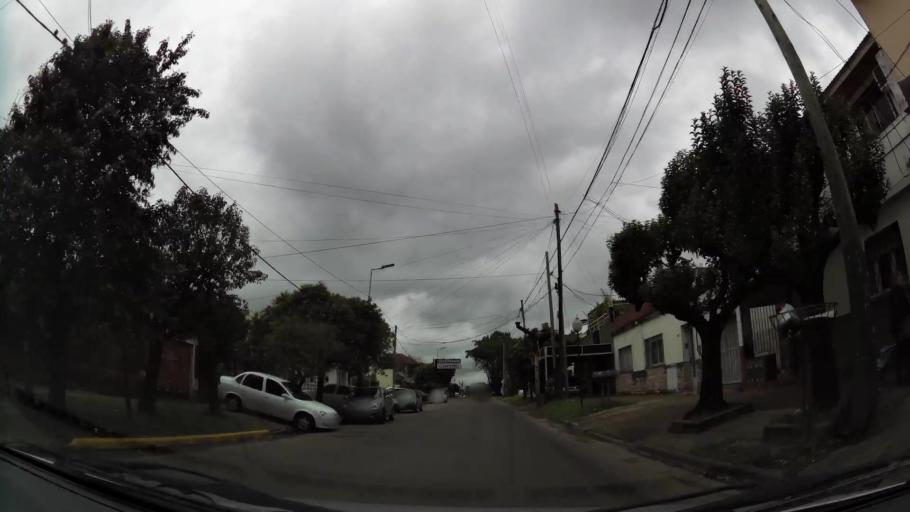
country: AR
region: Buenos Aires
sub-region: Partido de Lomas de Zamora
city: Lomas de Zamora
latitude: -34.7563
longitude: -58.3769
